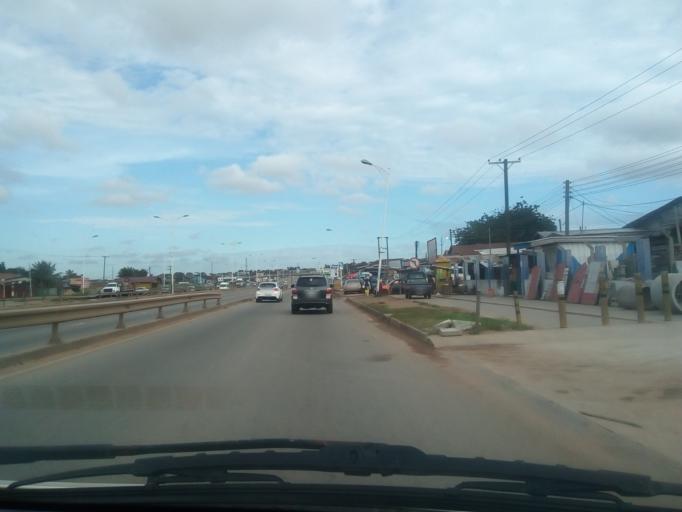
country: GH
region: Greater Accra
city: Dome
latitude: 5.6517
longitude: -0.2566
